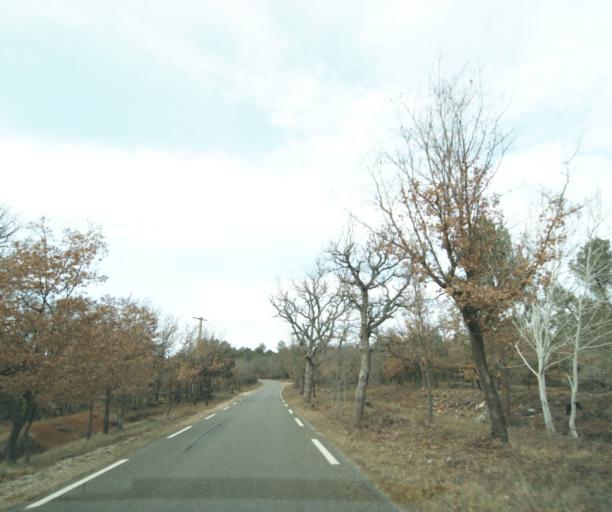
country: FR
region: Provence-Alpes-Cote d'Azur
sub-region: Departement du Var
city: Tourves
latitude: 43.3718
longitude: 5.9058
